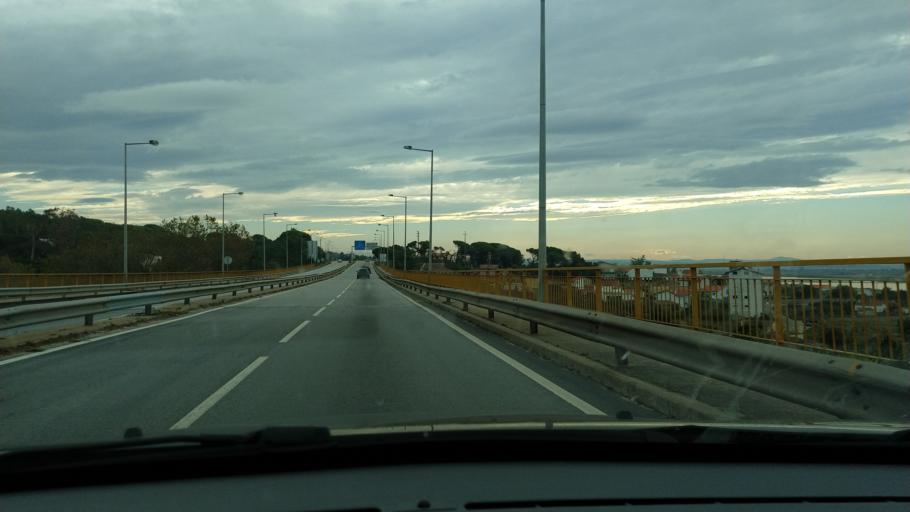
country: PT
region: Coimbra
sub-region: Figueira da Foz
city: Tavarede
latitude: 40.1510
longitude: -8.8385
